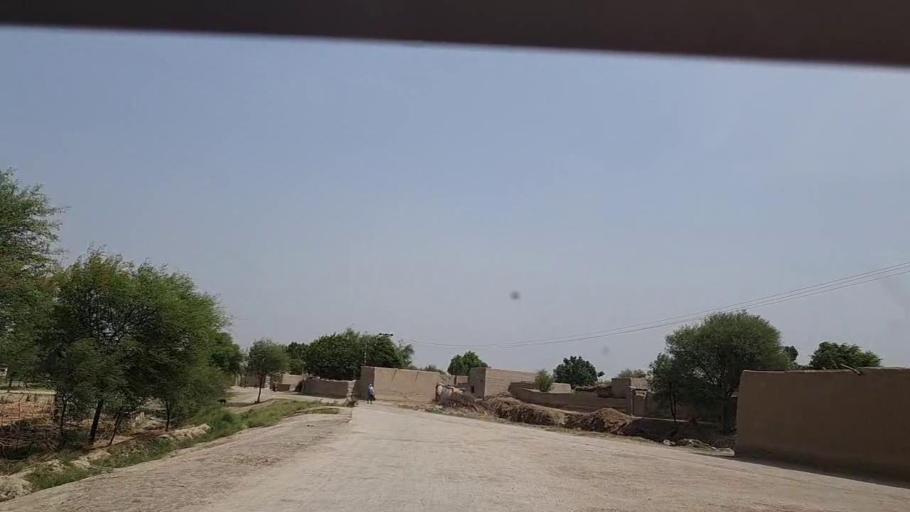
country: PK
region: Sindh
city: Khairpur Nathan Shah
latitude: 27.0822
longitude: 67.6651
